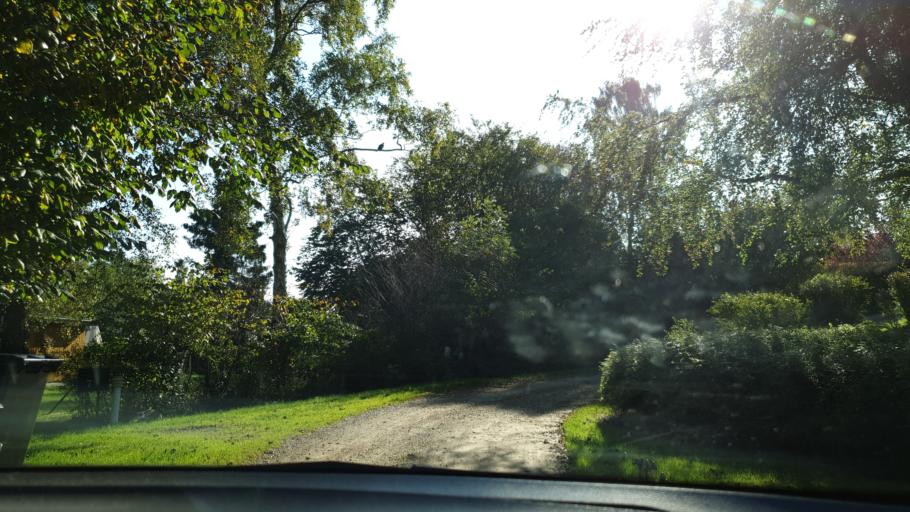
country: DK
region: Zealand
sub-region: Odsherred Kommune
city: Hojby
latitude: 55.9351
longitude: 11.6259
